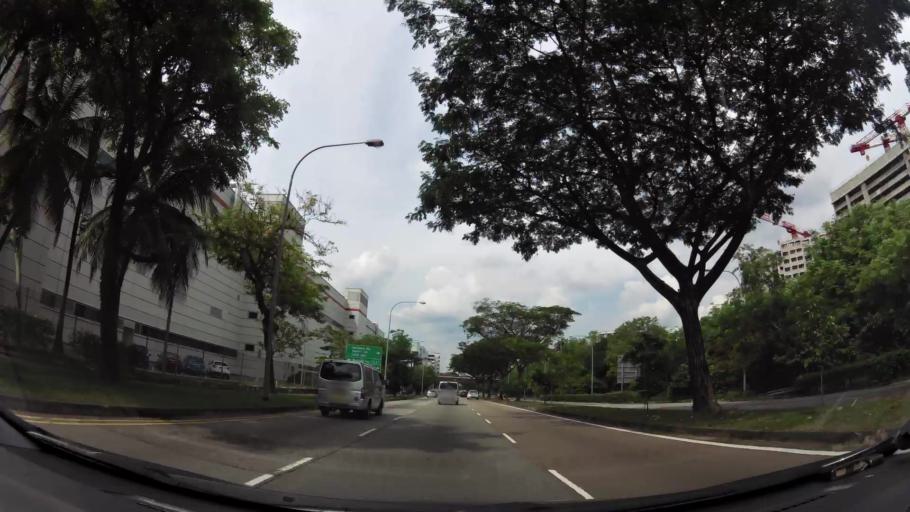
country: MY
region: Johor
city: Johor Bahru
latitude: 1.4454
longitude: 103.8118
